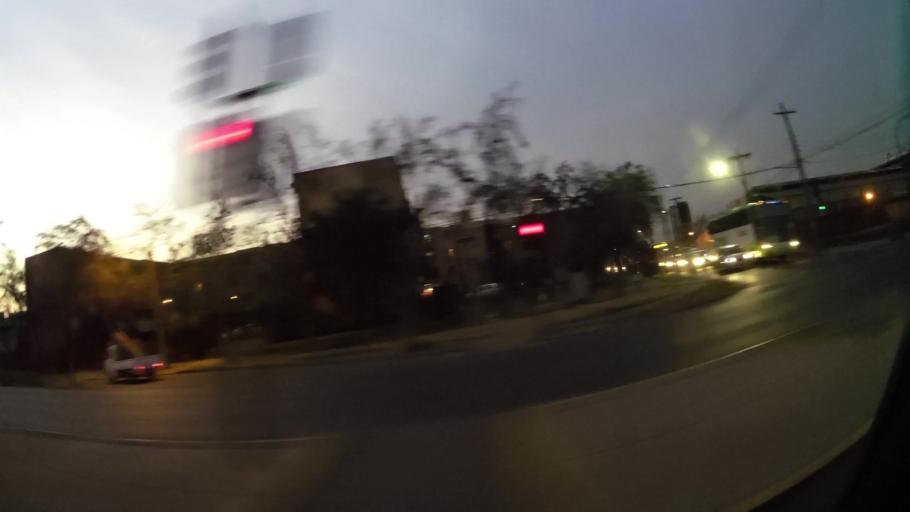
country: CL
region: Santiago Metropolitan
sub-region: Provincia de Santiago
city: Lo Prado
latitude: -33.4606
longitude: -70.6958
